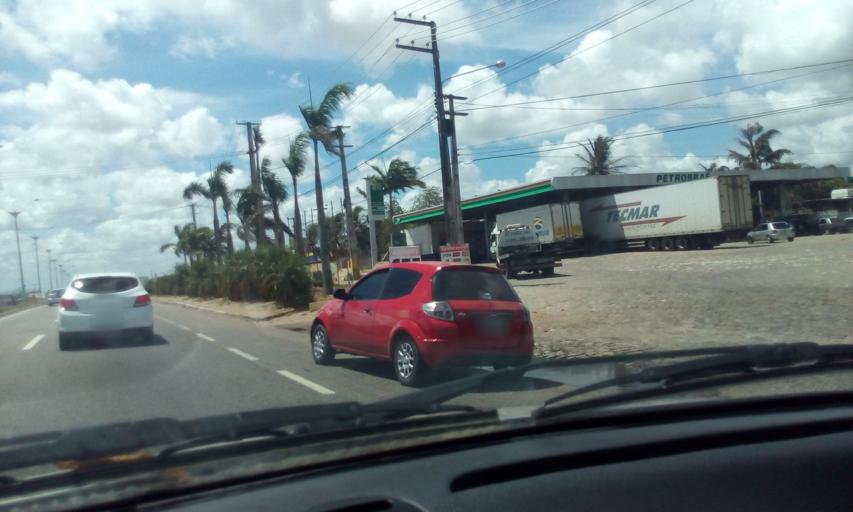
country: BR
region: Rio Grande do Norte
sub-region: Parnamirim
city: Parnamirim
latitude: -5.8944
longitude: -35.2578
